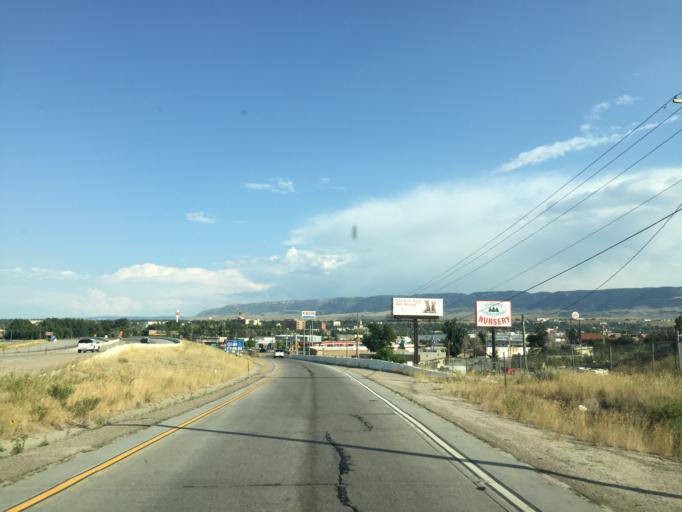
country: US
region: Wyoming
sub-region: Natrona County
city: Casper
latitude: 42.8591
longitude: -106.3367
